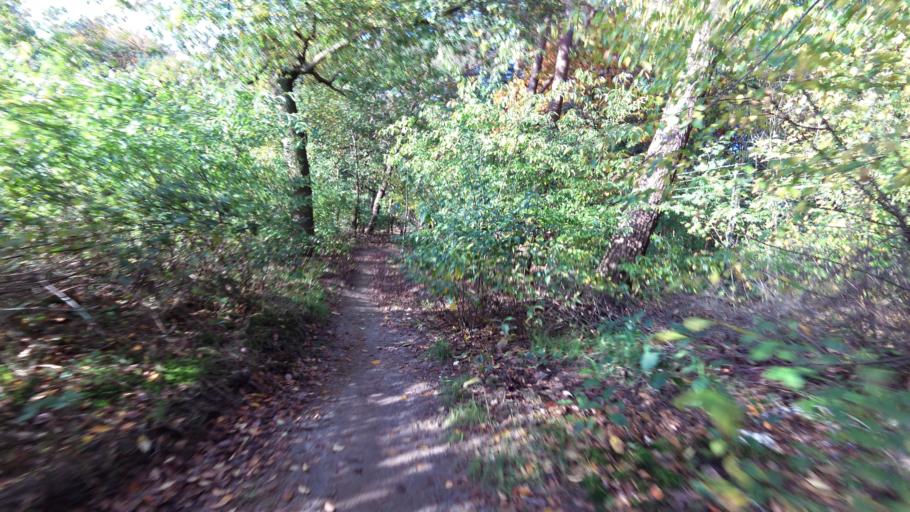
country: NL
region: Gelderland
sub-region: Gemeente Ede
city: Ede
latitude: 52.0660
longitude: 5.6639
